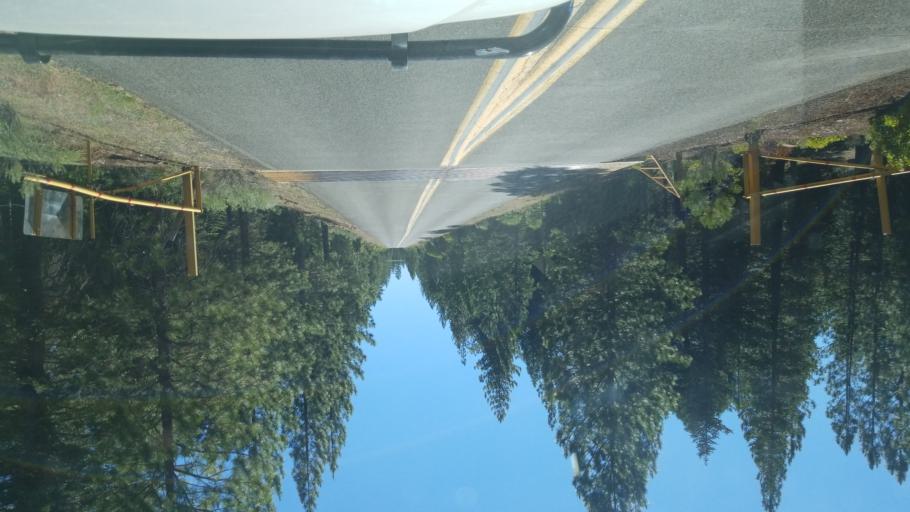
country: US
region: California
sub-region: Lassen County
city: Susanville
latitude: 40.5422
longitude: -120.7951
